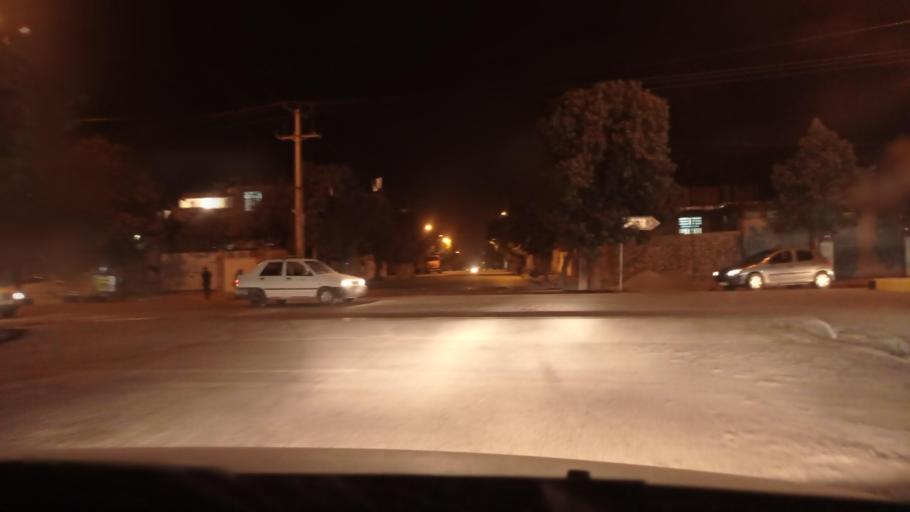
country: IR
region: Lorestan
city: Kuhdasht
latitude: 33.5376
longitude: 47.6115
